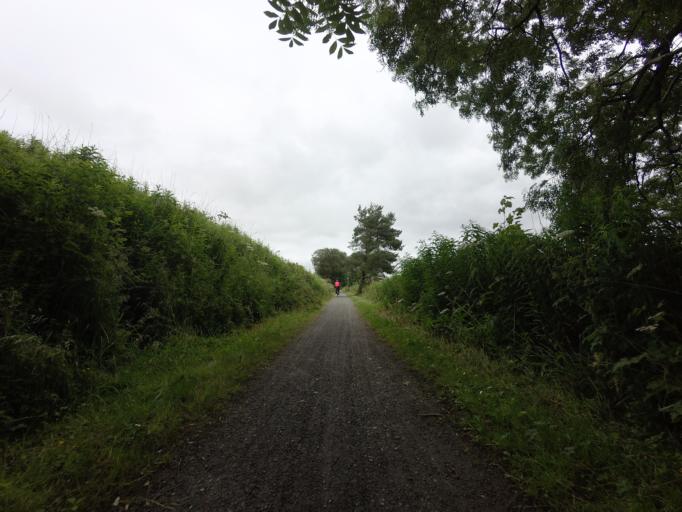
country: GB
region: Scotland
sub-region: Aberdeenshire
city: Mintlaw
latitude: 57.5137
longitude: -2.1383
